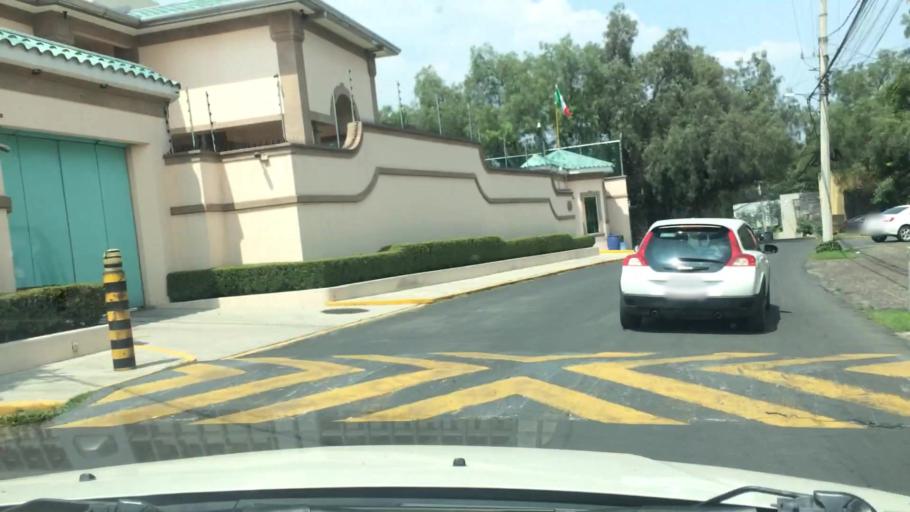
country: MX
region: Mexico City
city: Magdalena Contreras
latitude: 19.3292
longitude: -99.2049
